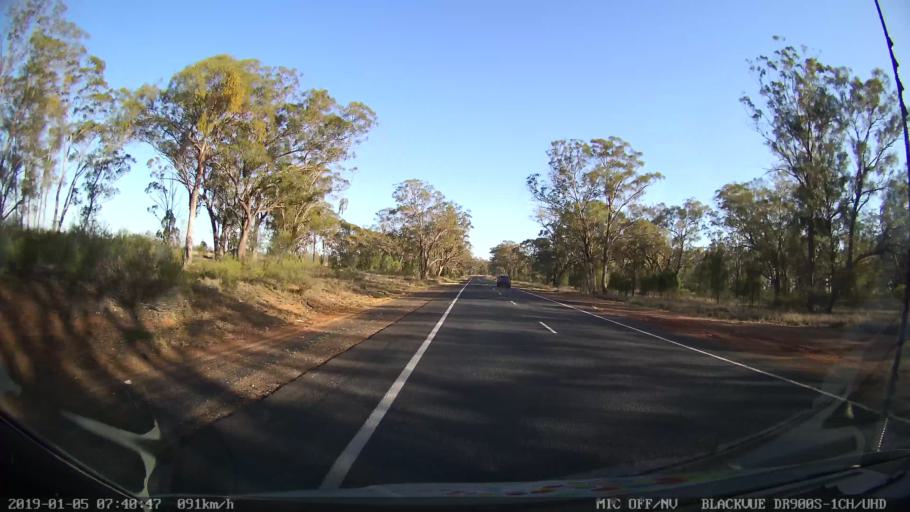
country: AU
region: New South Wales
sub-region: Gilgandra
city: Gilgandra
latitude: -31.9193
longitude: 148.6192
